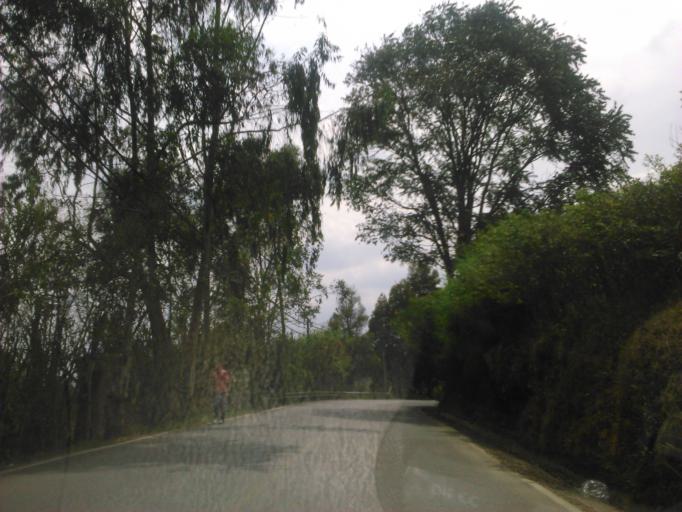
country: CO
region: Antioquia
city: San Vicente
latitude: 6.2324
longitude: -75.3800
